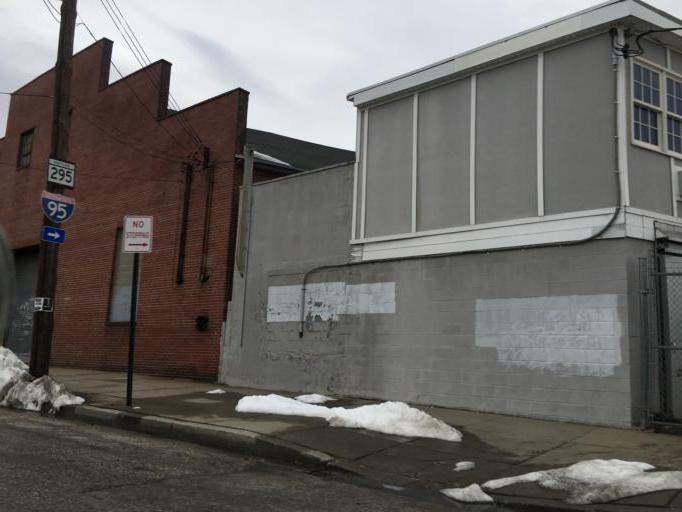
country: US
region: Maryland
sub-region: City of Baltimore
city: Baltimore
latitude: 39.2777
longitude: -76.6285
